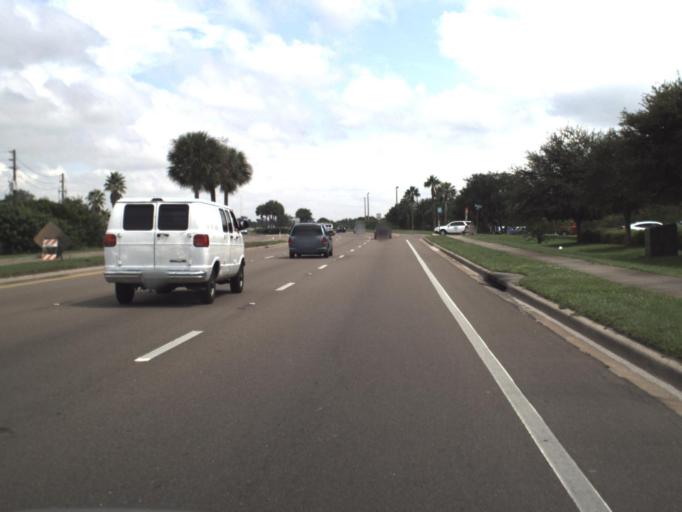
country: US
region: Florida
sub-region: Manatee County
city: Ellenton
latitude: 27.4960
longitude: -82.5288
